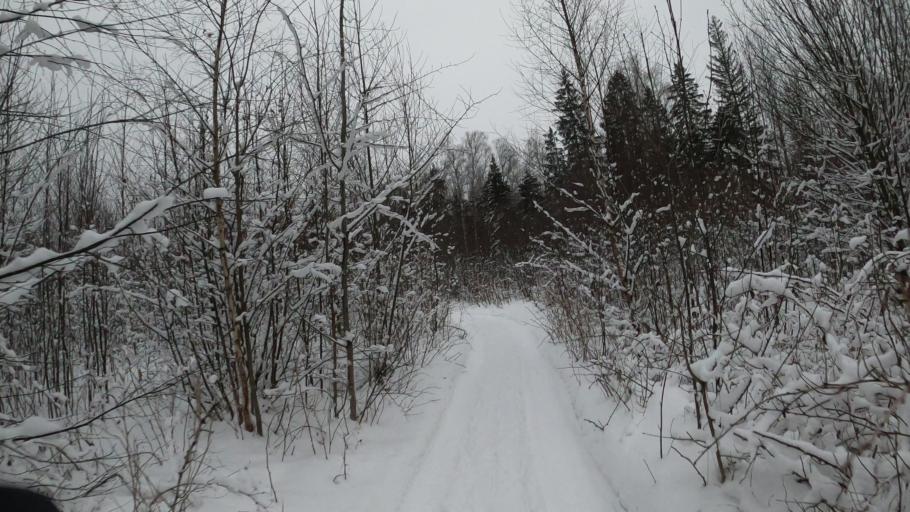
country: RU
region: Moskovskaya
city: Firsanovka
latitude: 55.9107
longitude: 37.2036
